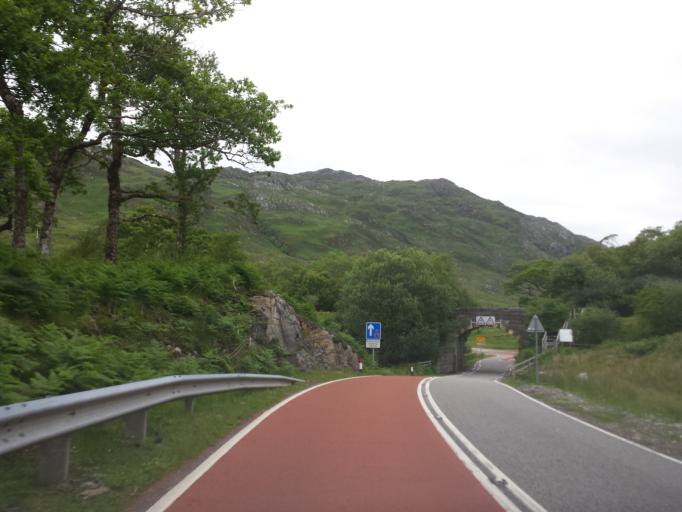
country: GB
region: Scotland
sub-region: Argyll and Bute
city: Isle Of Mull
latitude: 56.8994
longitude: -5.7550
